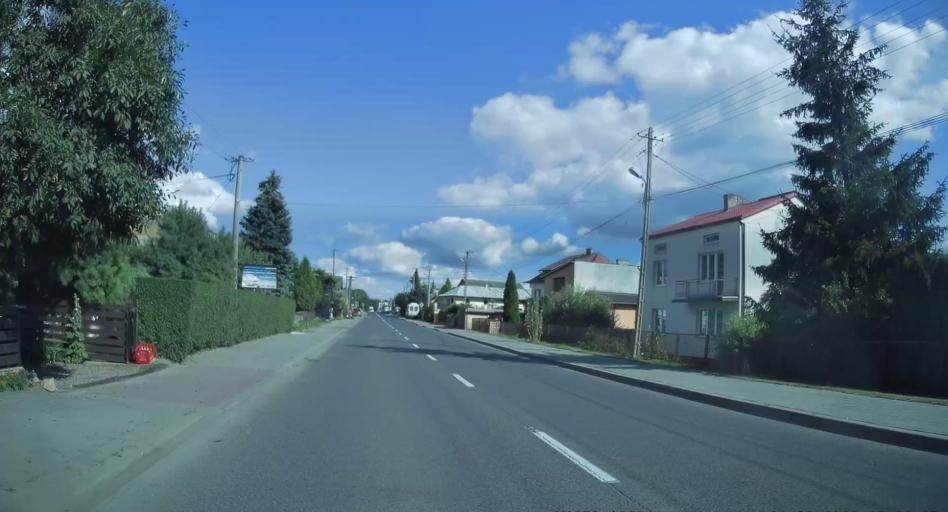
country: PL
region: Swietokrzyskie
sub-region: Powiat kielecki
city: Bodzentyn
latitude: 50.9443
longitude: 20.9418
